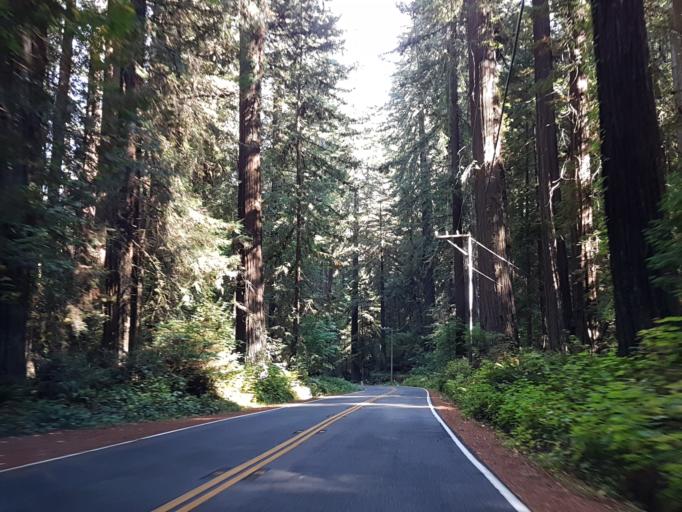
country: US
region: California
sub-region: Humboldt County
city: Rio Dell
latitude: 40.4164
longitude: -123.9718
